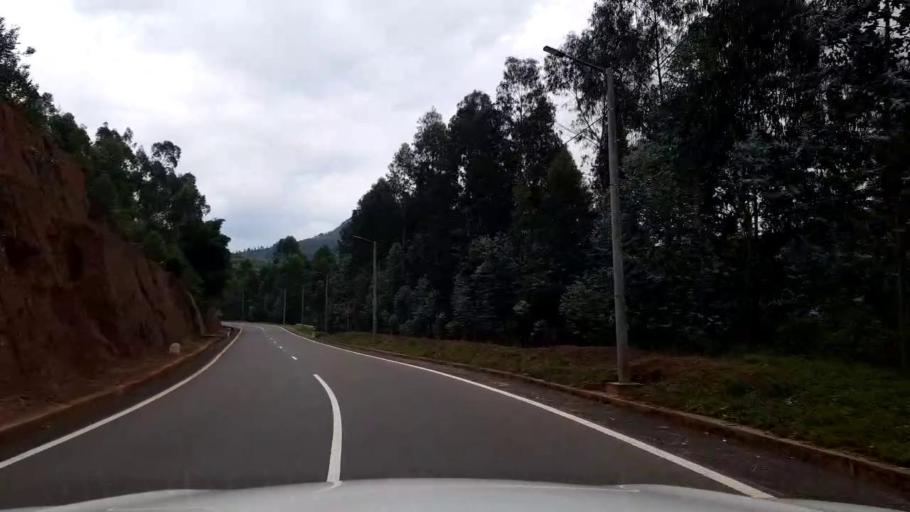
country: RW
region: Western Province
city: Kibuye
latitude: -1.9231
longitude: 29.3688
